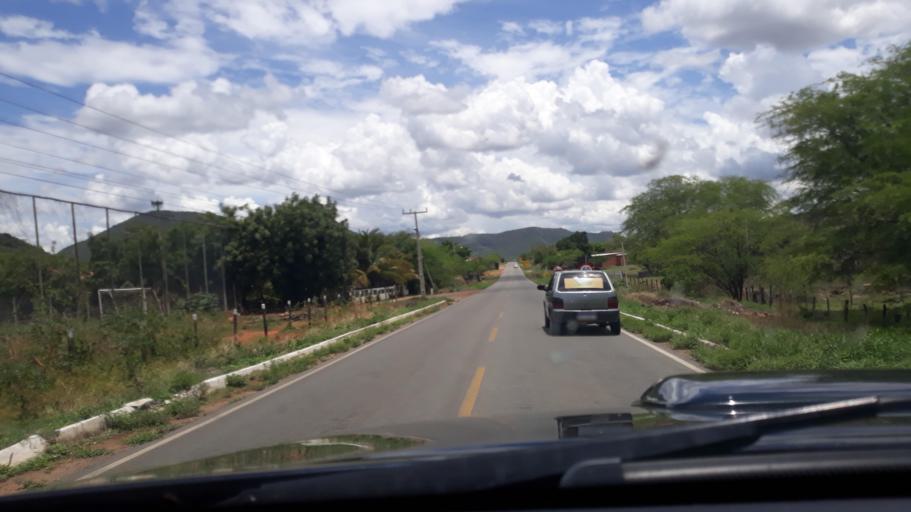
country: BR
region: Bahia
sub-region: Guanambi
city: Guanambi
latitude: -14.2658
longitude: -42.7177
